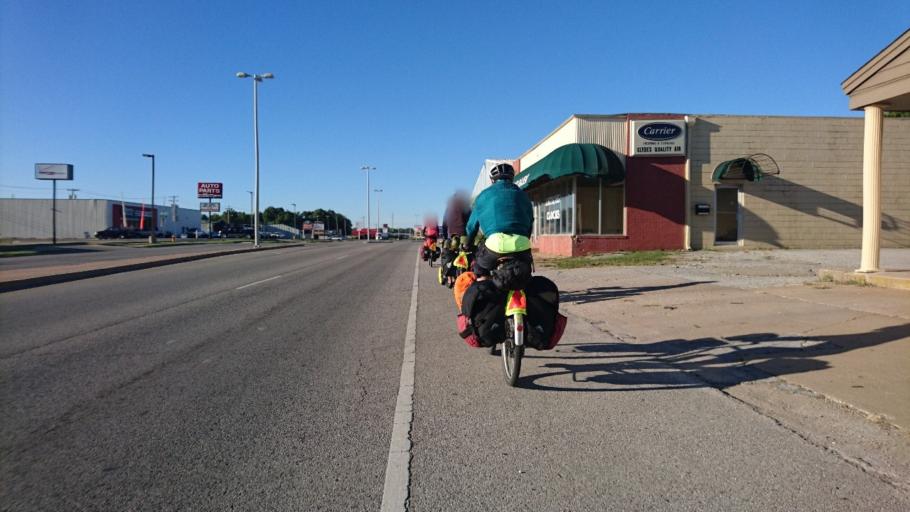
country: US
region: Oklahoma
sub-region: Rogers County
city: Claremore
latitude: 36.3103
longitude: -95.6176
